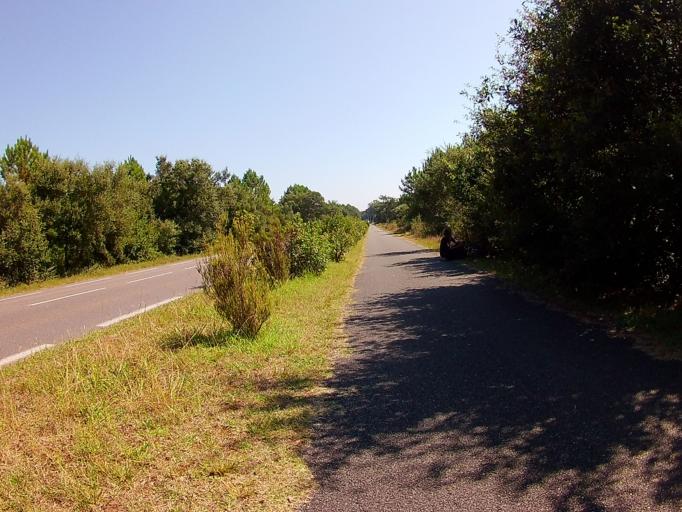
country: FR
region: Aquitaine
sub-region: Departement des Landes
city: Labenne
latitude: 43.5936
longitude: -1.4524
